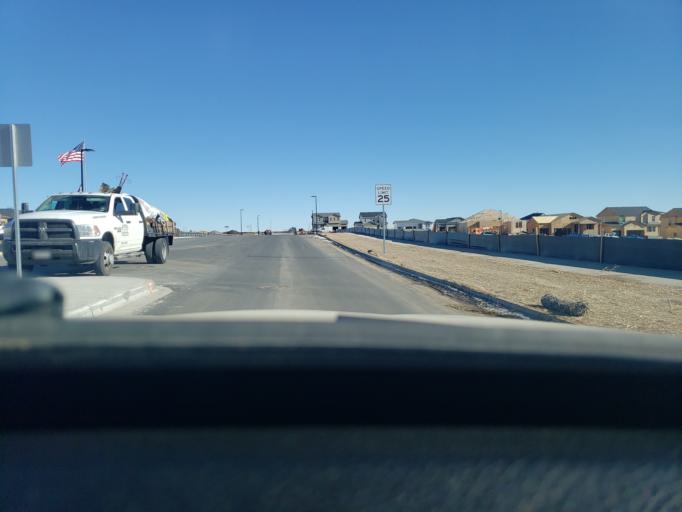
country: US
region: Colorado
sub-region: Adams County
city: Aurora
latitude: 39.7728
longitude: -104.7061
